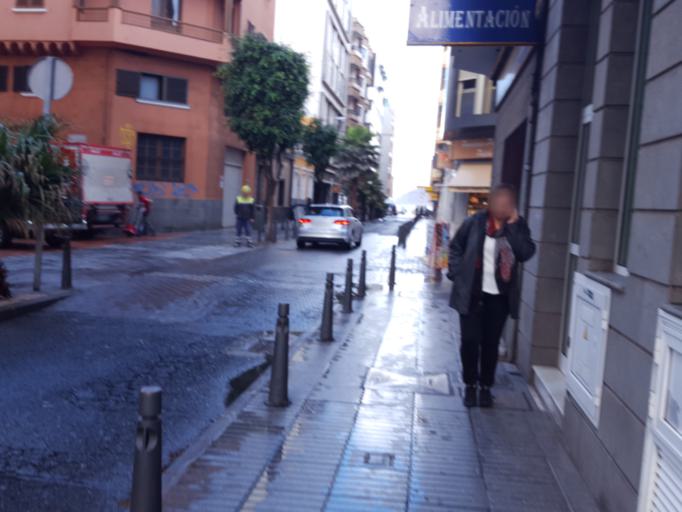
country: ES
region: Canary Islands
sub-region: Provincia de Las Palmas
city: Las Palmas de Gran Canaria
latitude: 28.1385
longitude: -15.4356
